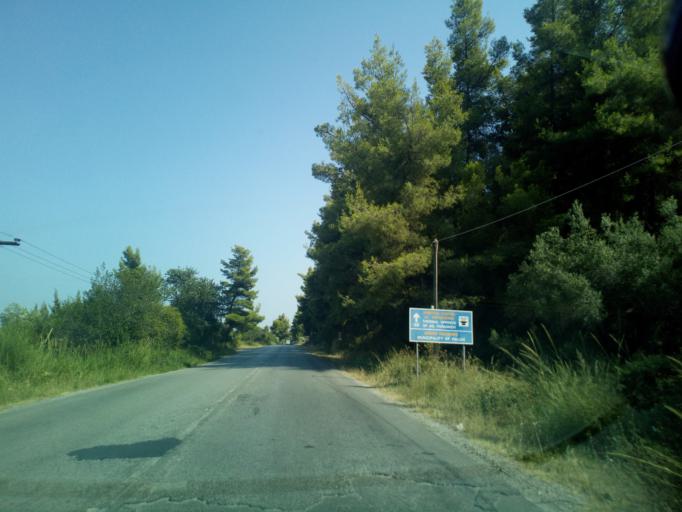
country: GR
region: Central Macedonia
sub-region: Nomos Chalkidikis
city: Kallithea
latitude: 40.0262
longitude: 23.5050
